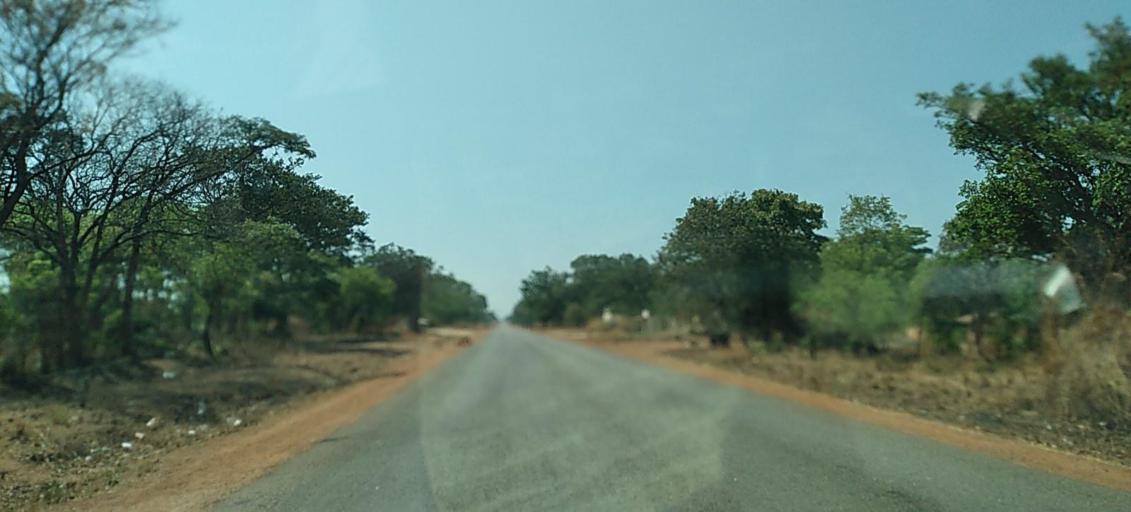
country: ZM
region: North-Western
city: Solwezi
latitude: -12.2788
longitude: 25.6823
